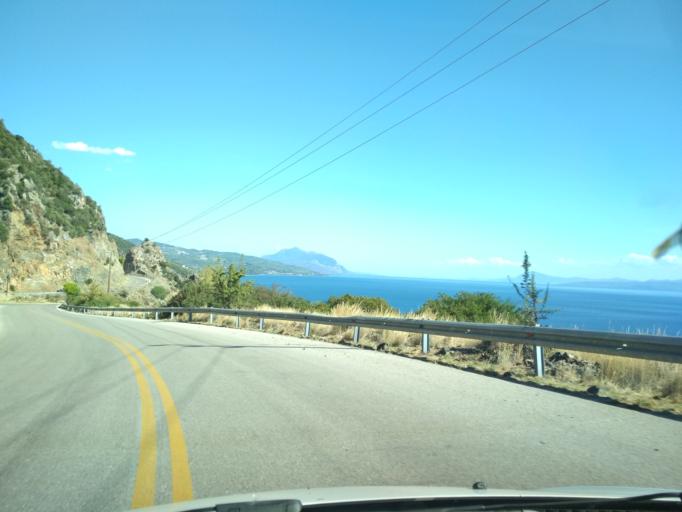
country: GR
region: Central Greece
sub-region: Nomos Evvoias
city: Roviai
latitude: 38.8482
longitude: 23.1534
